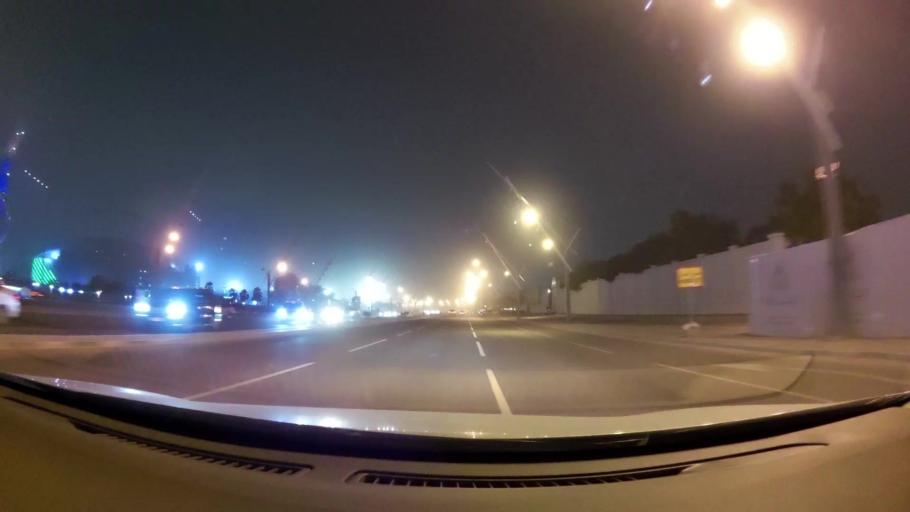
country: QA
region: Baladiyat ar Rayyan
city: Ar Rayyan
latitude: 25.2619
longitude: 51.4539
